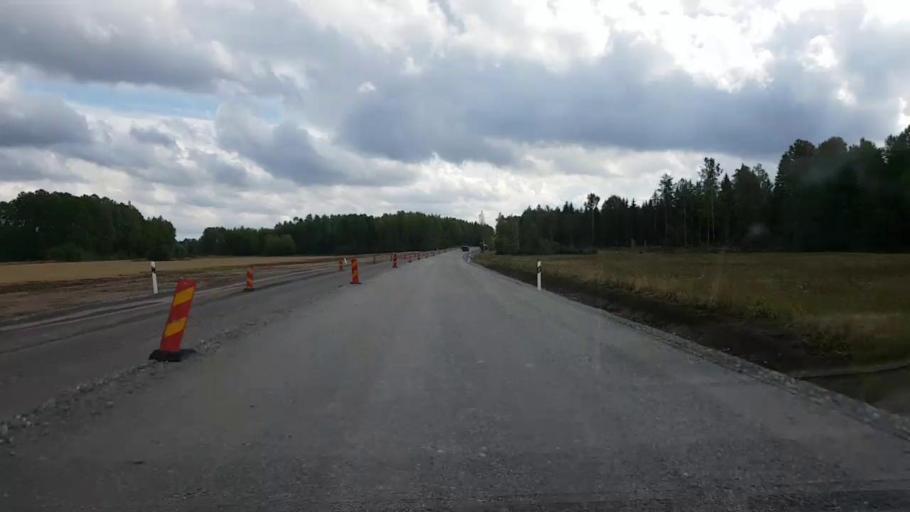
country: SE
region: Uppsala
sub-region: Enkopings Kommun
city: Enkoping
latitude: 59.6672
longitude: 17.0681
